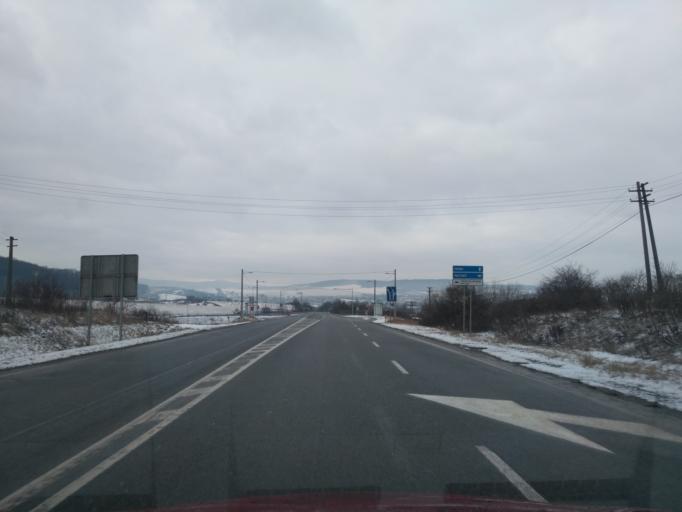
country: SK
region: Presovsky
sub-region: Okres Presov
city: Presov
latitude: 49.0014
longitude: 21.1929
